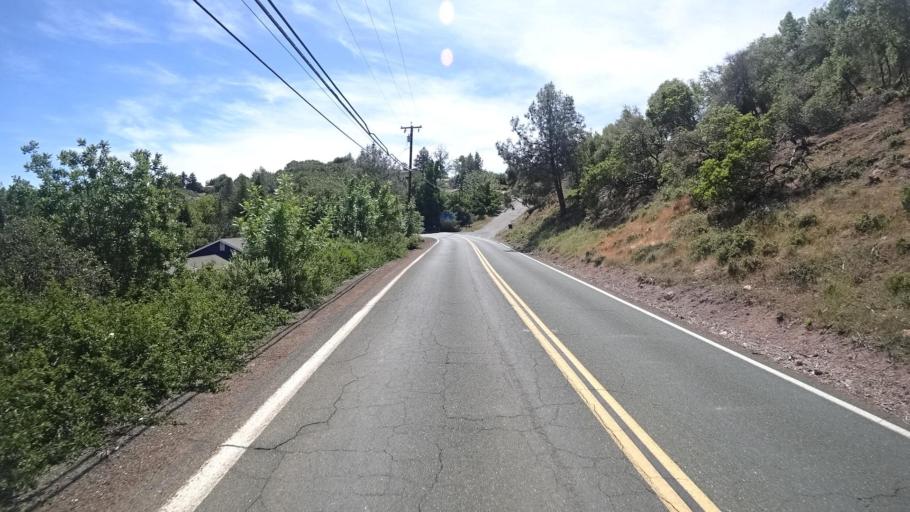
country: US
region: California
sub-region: Lake County
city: Clearlake Oaks
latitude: 38.9537
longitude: -122.7169
